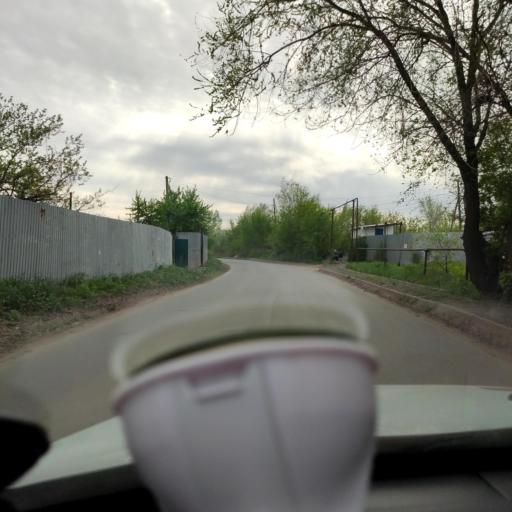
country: RU
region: Samara
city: Smyshlyayevka
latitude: 53.2157
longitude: 50.3303
